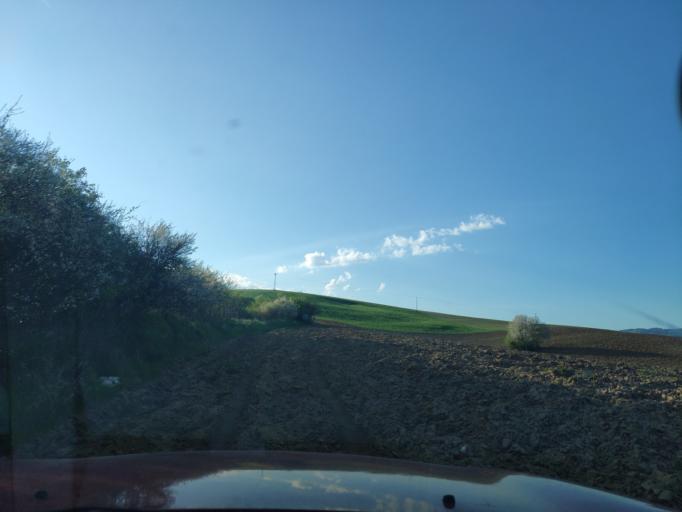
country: SK
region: Presovsky
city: Lipany
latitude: 49.1495
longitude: 20.8594
